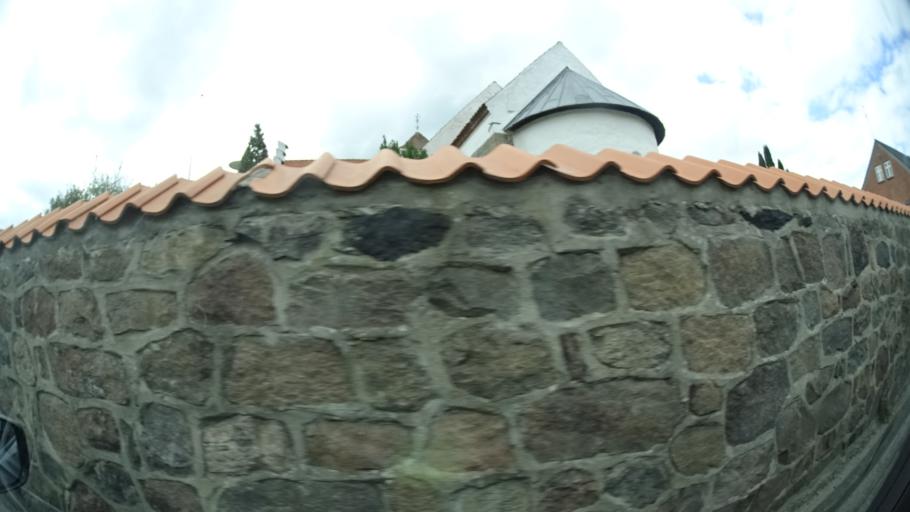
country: DK
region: Central Jutland
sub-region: Syddjurs Kommune
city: Ryomgard
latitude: 56.4083
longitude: 10.5665
